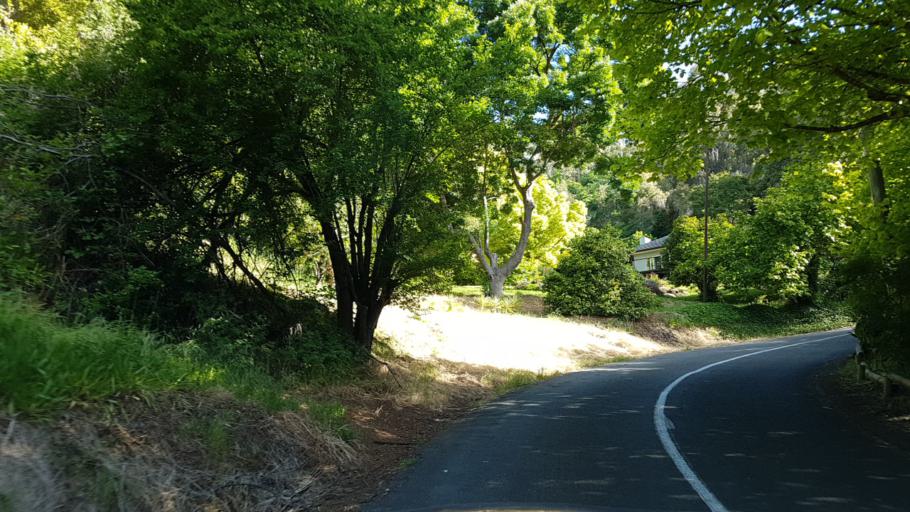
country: AU
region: South Australia
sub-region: Adelaide Hills
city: Adelaide Hills
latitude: -34.9099
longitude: 138.7724
